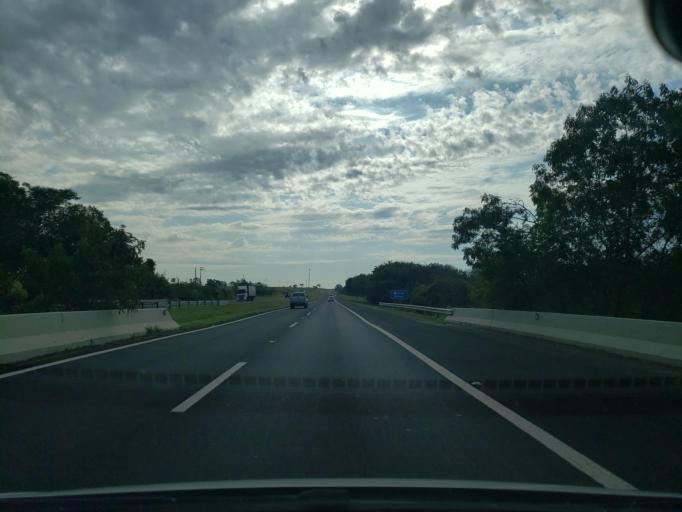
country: BR
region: Sao Paulo
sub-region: Birigui
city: Birigui
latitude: -21.3490
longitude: -50.3142
